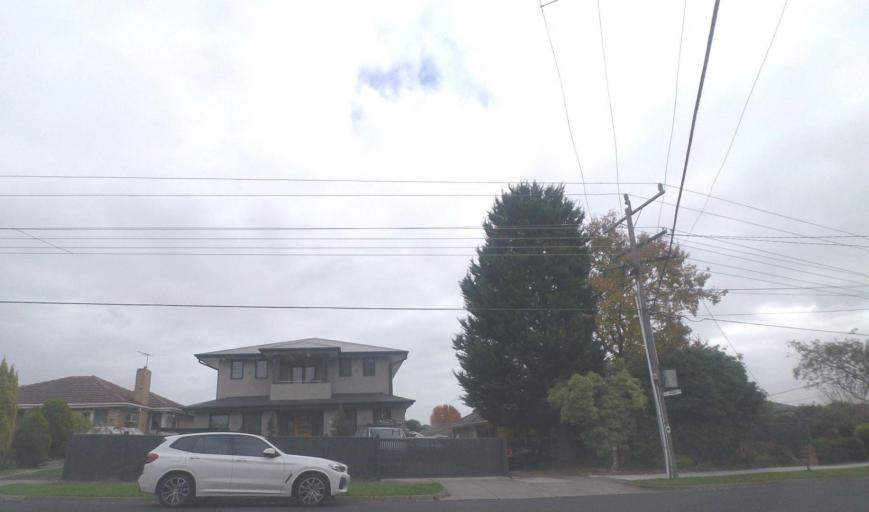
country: AU
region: Victoria
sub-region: Whitehorse
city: Blackburn North
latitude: -37.8070
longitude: 145.1492
